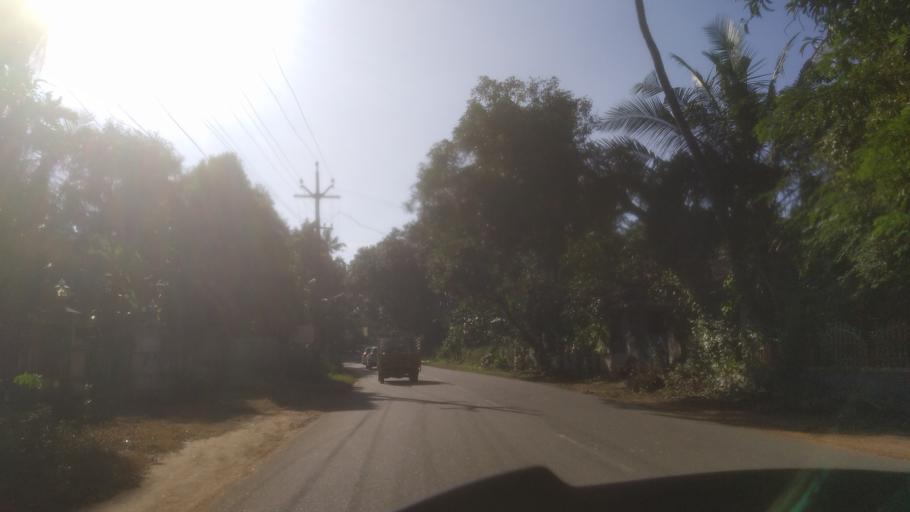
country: IN
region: Kerala
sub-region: Ernakulam
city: Muvattupuzha
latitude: 9.9764
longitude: 76.5313
